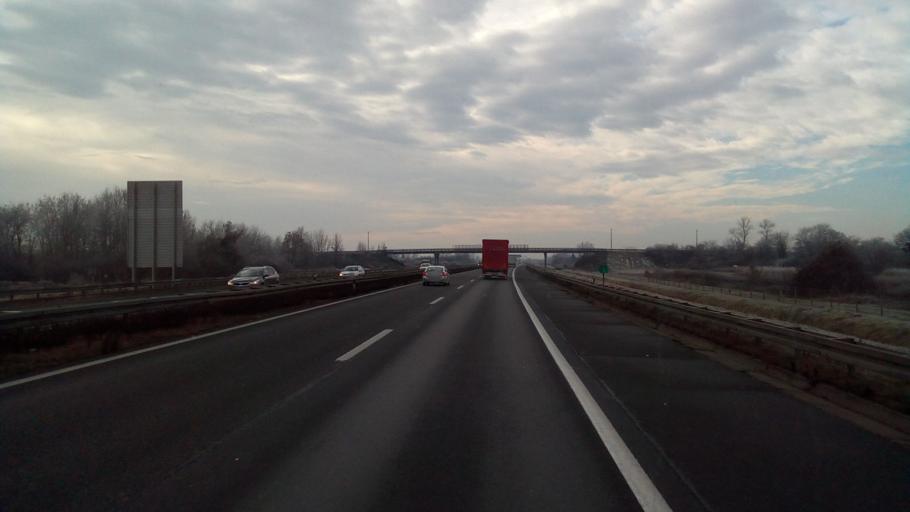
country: HR
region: Grad Zagreb
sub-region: Sesvete
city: Sesvete
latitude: 45.7794
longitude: 16.1134
